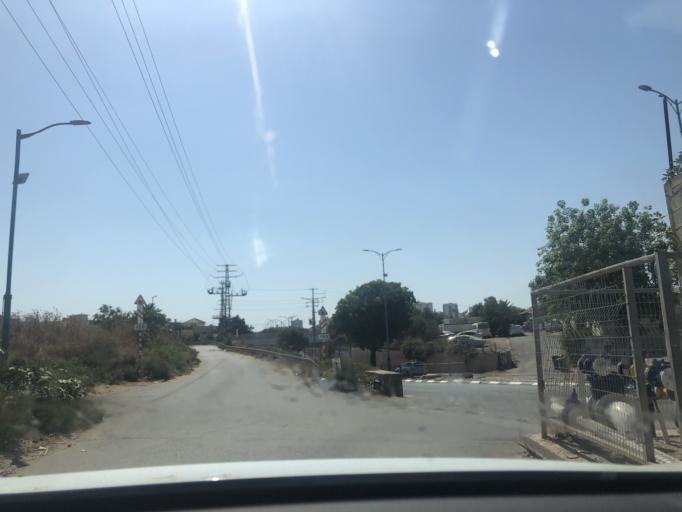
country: IL
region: Central District
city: Lod
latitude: 31.9574
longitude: 34.8895
